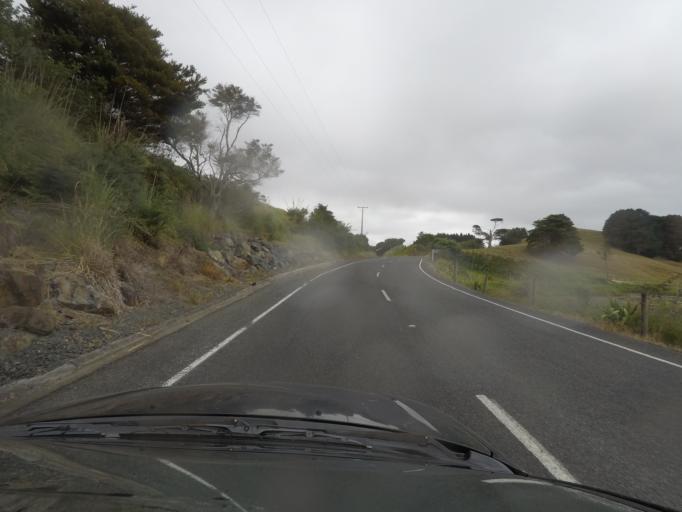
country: NZ
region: Auckland
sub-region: Auckland
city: Warkworth
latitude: -36.2650
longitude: 174.7121
